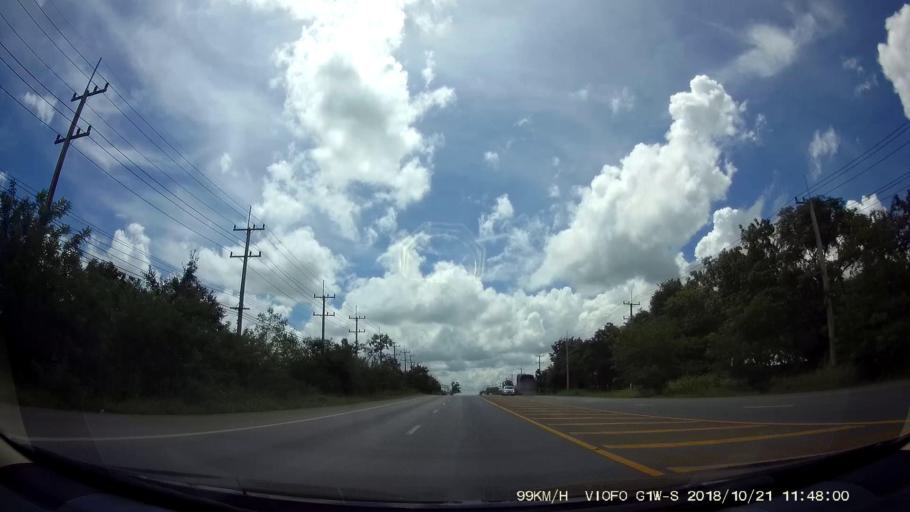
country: TH
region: Chaiyaphum
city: Noen Sa-nga
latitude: 15.6536
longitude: 101.9514
